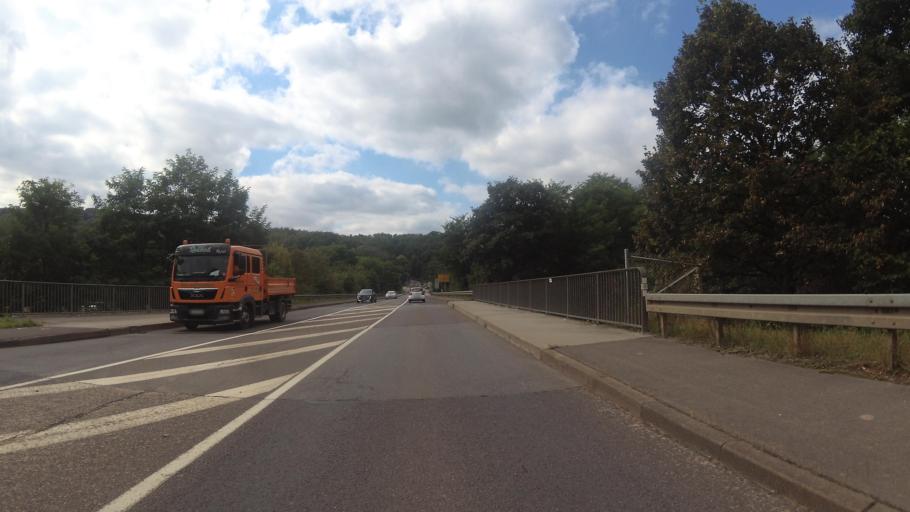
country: DE
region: Saarland
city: Grossrosseln
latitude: 49.2165
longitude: 6.8301
